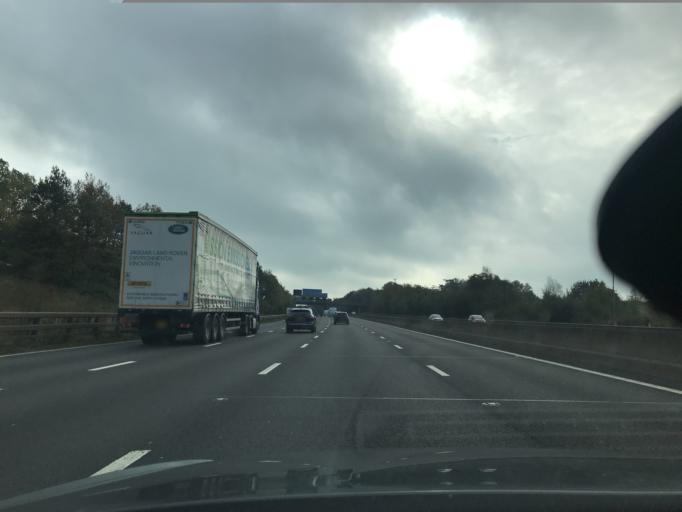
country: GB
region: England
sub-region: Staffordshire
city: Penkridge
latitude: 52.6932
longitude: -2.1051
